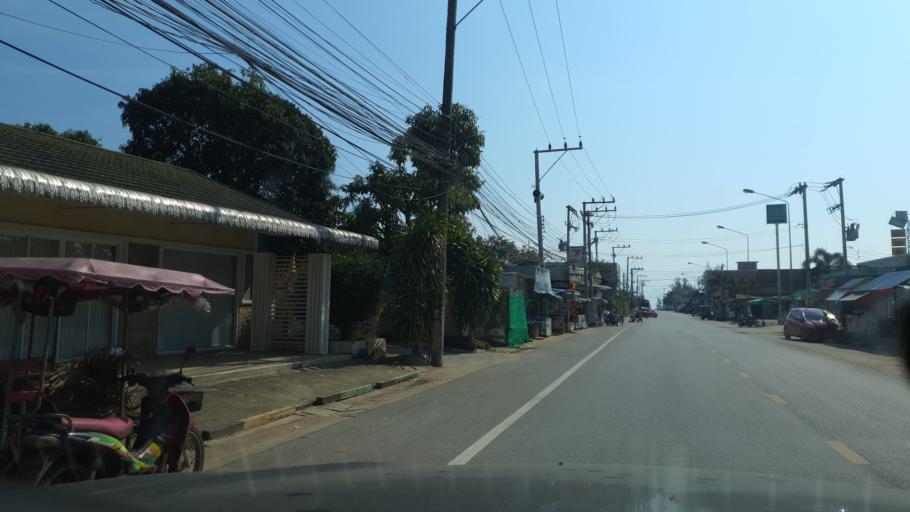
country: TH
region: Prachuap Khiri Khan
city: Bang Saphan
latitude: 11.3462
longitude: 99.5613
